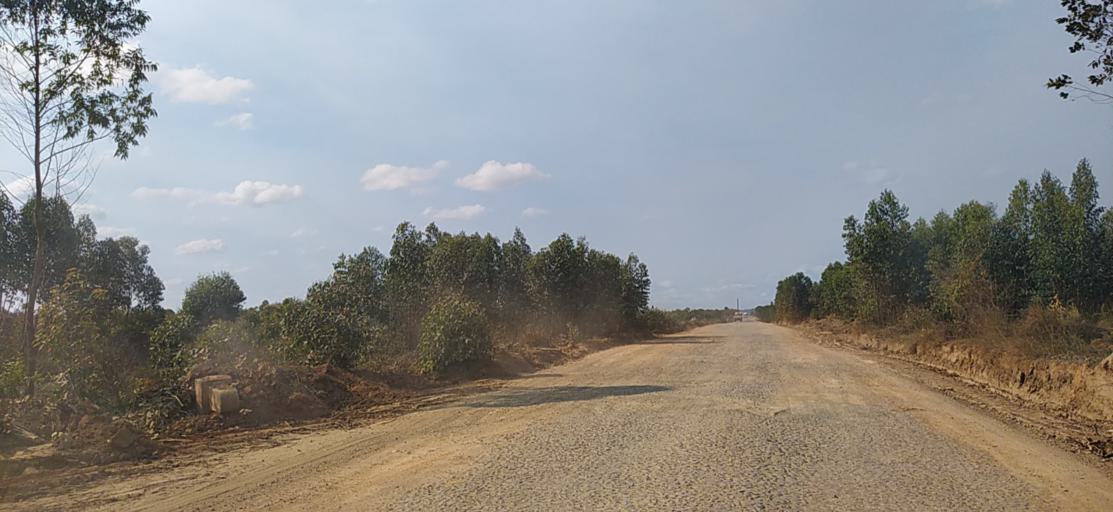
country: MG
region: Alaotra Mangoro
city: Moramanga
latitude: -18.6872
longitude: 48.2712
